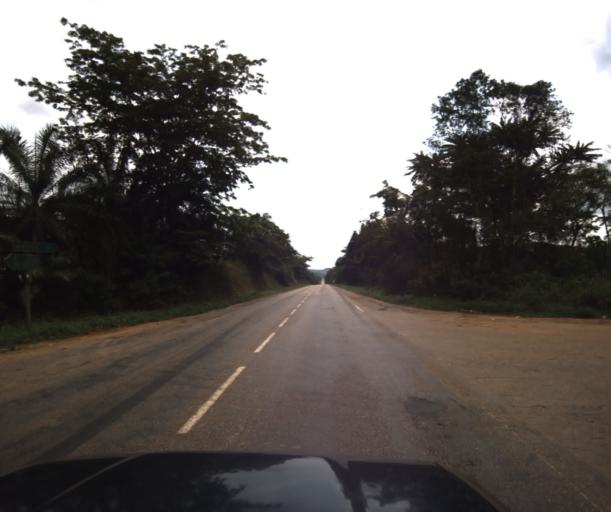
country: CM
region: Centre
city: Eseka
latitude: 3.8508
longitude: 10.5105
